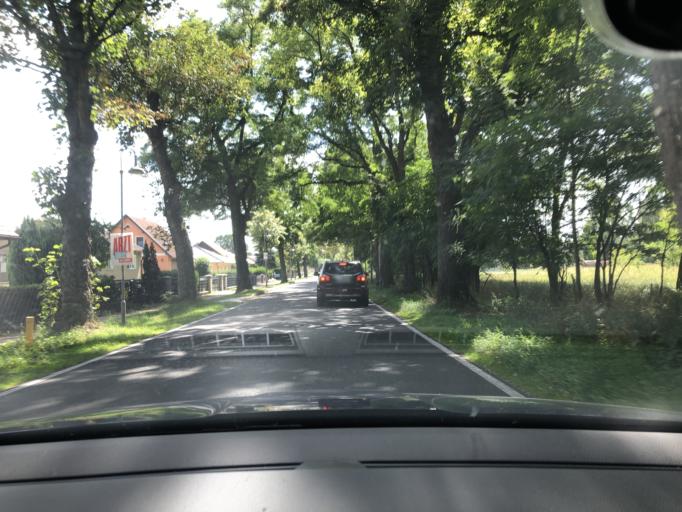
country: DE
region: Brandenburg
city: Kremmen
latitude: 52.8185
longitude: 13.0181
